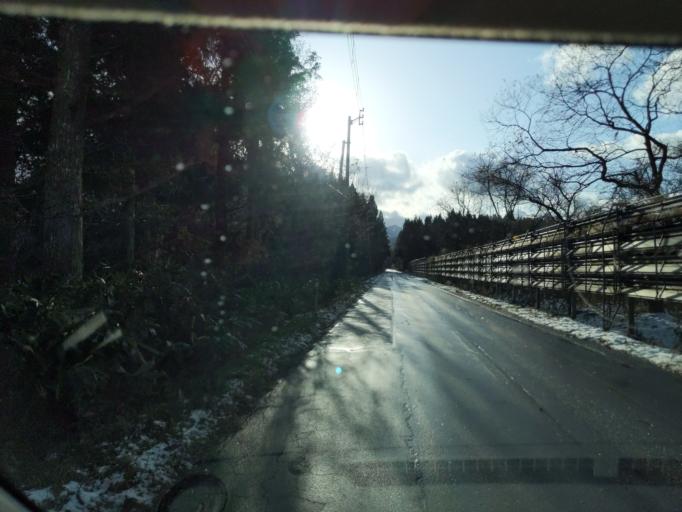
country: JP
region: Iwate
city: Kitakami
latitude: 39.2482
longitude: 141.0104
